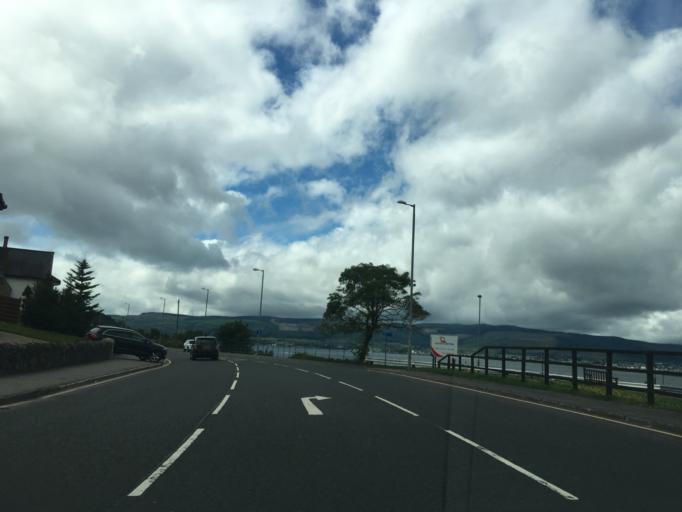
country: GB
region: Scotland
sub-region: Inverclyde
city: Gourock
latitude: 55.9510
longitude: -4.8532
